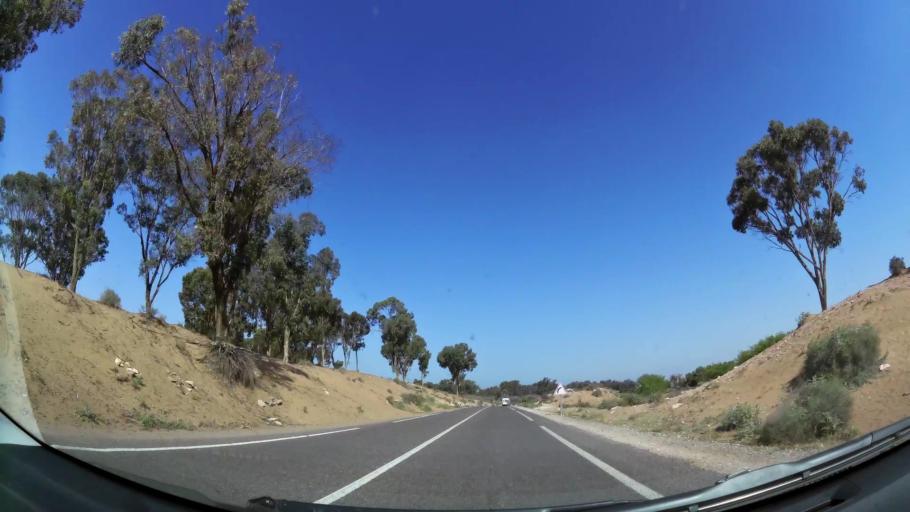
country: MA
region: Souss-Massa-Draa
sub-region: Inezgane-Ait Mellou
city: Inezgane
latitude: 30.3166
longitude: -9.5244
